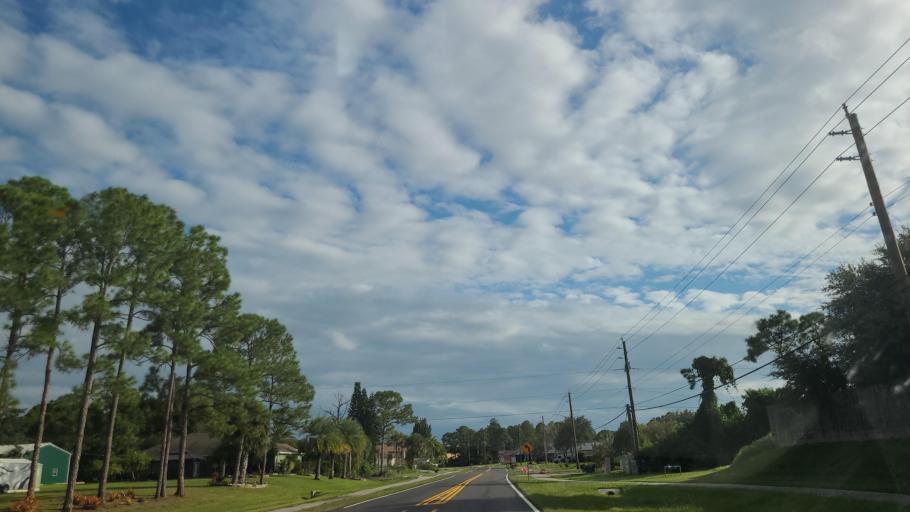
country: US
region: Florida
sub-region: Brevard County
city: June Park
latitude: 27.9976
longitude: -80.6971
